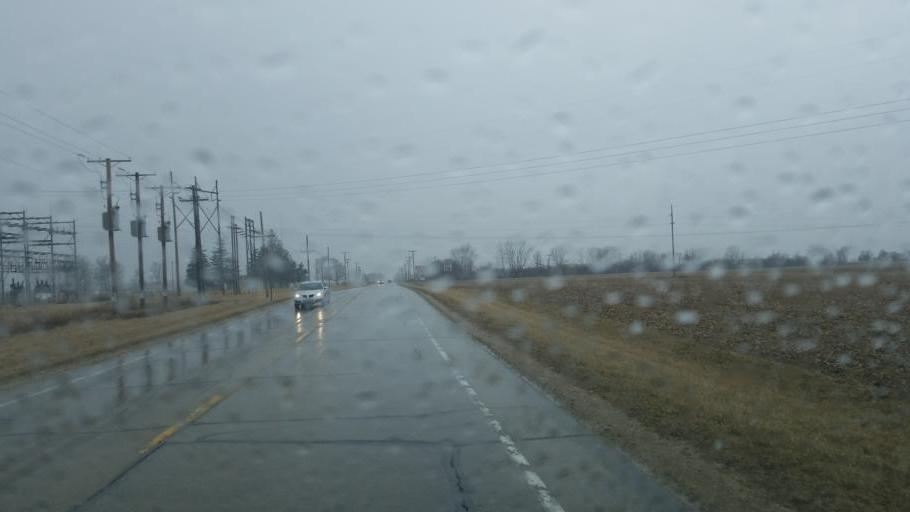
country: US
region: Indiana
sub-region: Adams County
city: Berne
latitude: 40.6558
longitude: -85.0434
